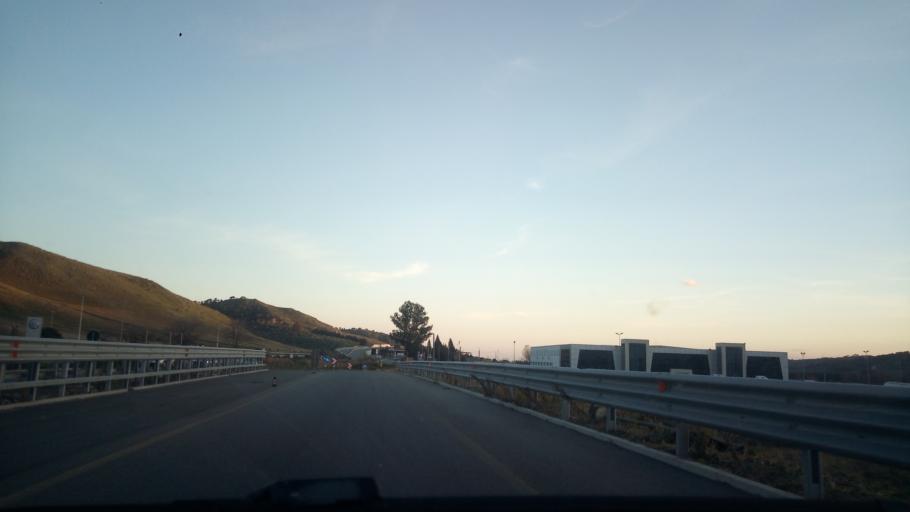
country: IT
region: Calabria
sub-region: Provincia di Catanzaro
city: Roccelletta
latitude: 38.8456
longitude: 16.5825
